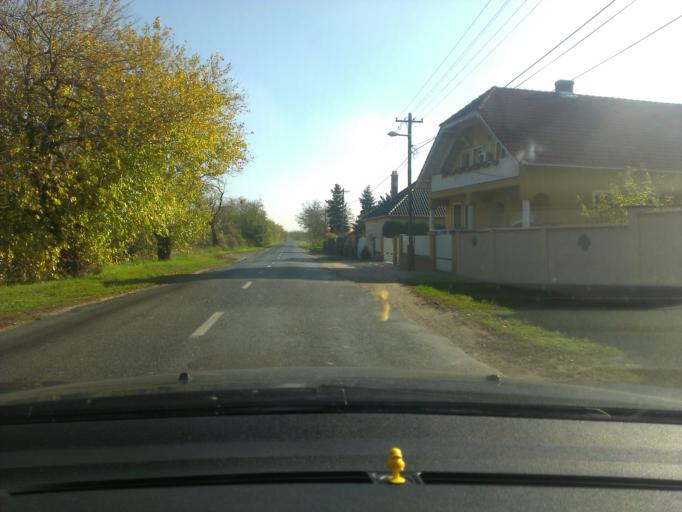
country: HU
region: Komarom-Esztergom
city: Komarom
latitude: 47.7232
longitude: 18.1677
